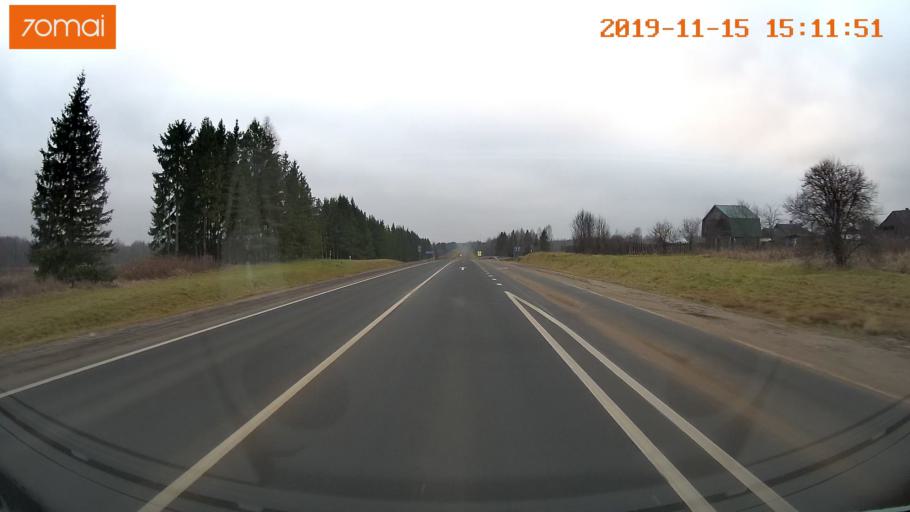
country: RU
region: Jaroslavl
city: Prechistoye
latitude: 58.3311
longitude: 40.2351
